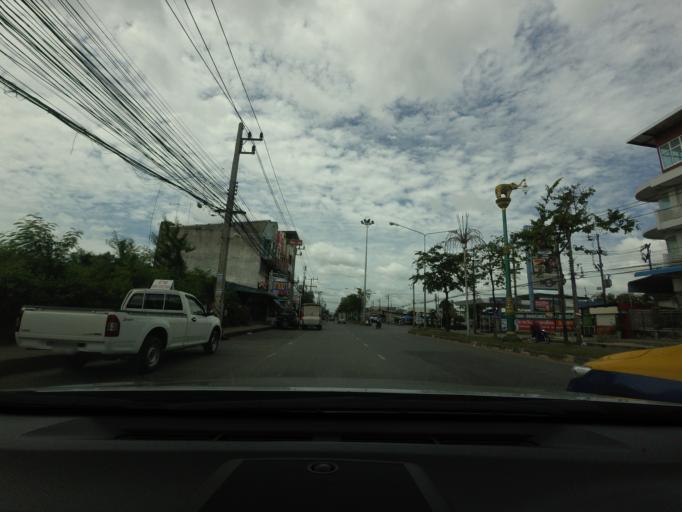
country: TH
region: Songkhla
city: Hat Yai
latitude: 7.0128
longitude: 100.4572
